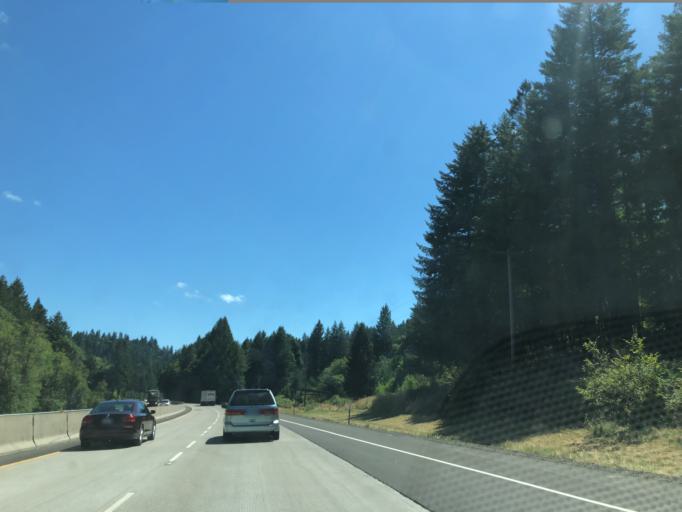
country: US
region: Oregon
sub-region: Douglas County
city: Yoncalla
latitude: 43.6686
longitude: -123.2030
